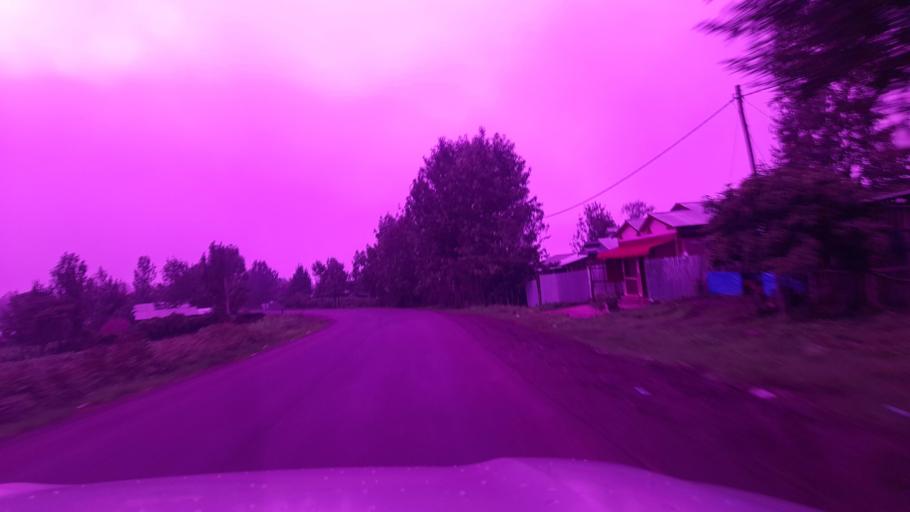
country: ET
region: Oromiya
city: Waliso
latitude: 8.1744
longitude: 37.5659
